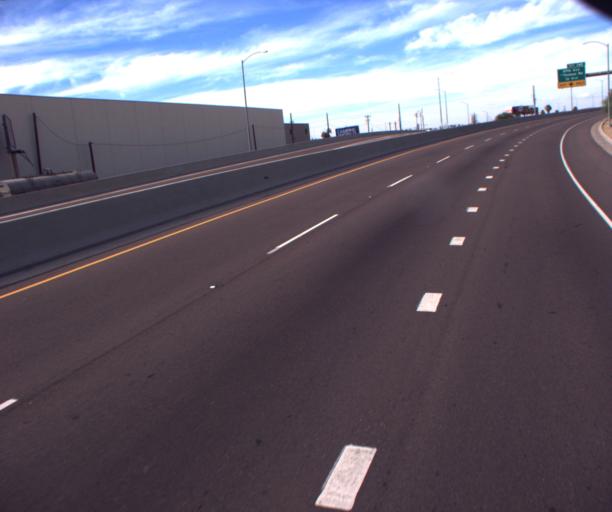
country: US
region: Arizona
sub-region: Maricopa County
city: Phoenix
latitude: 33.4781
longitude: -112.1141
